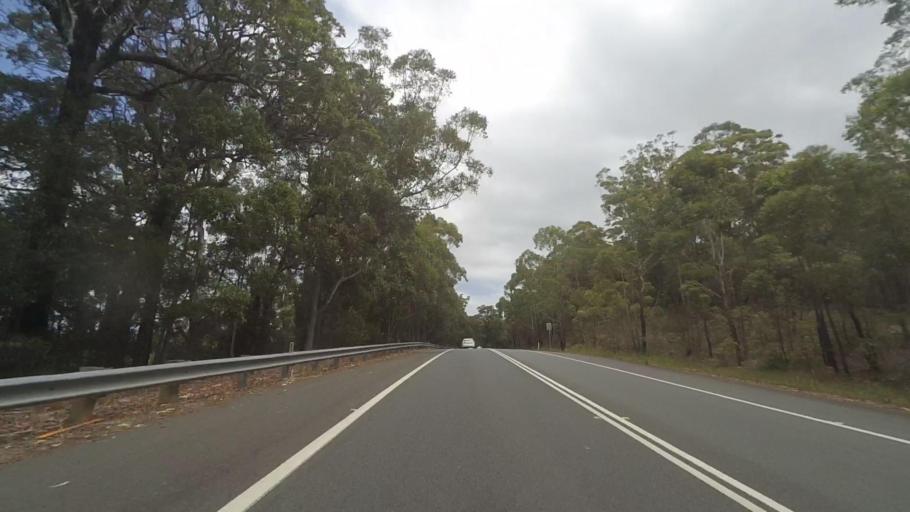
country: AU
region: New South Wales
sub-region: Shoalhaven Shire
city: Milton
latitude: -35.1512
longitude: 150.4560
